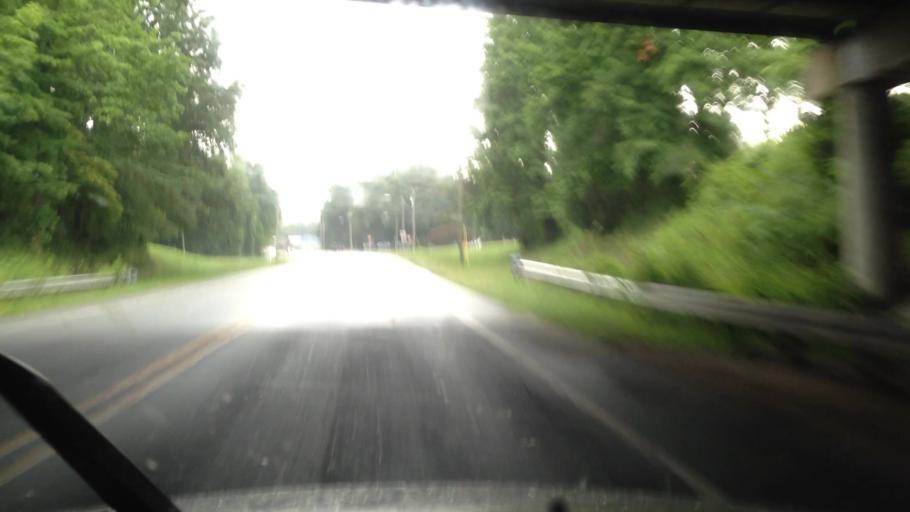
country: US
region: North Carolina
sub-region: Guilford County
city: Greensboro
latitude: 36.0549
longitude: -79.8543
